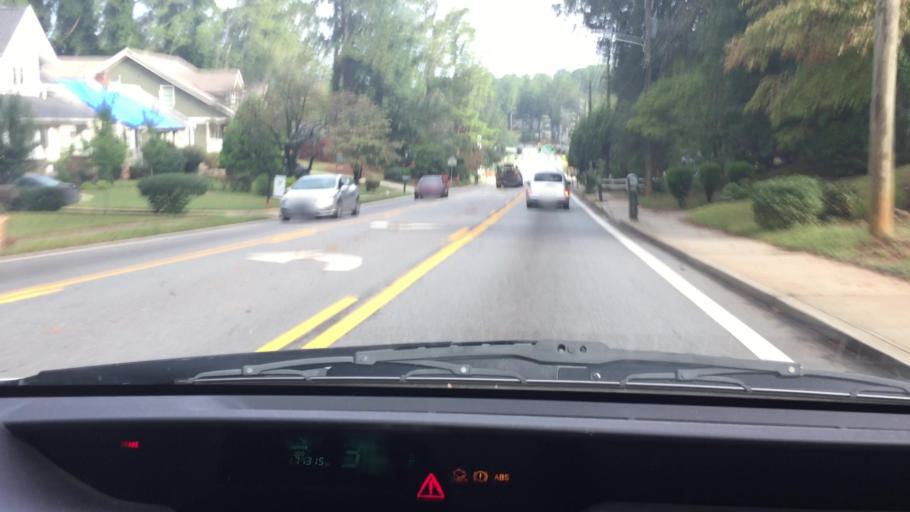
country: US
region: Georgia
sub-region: DeKalb County
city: Decatur
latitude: 33.7547
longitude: -84.2916
